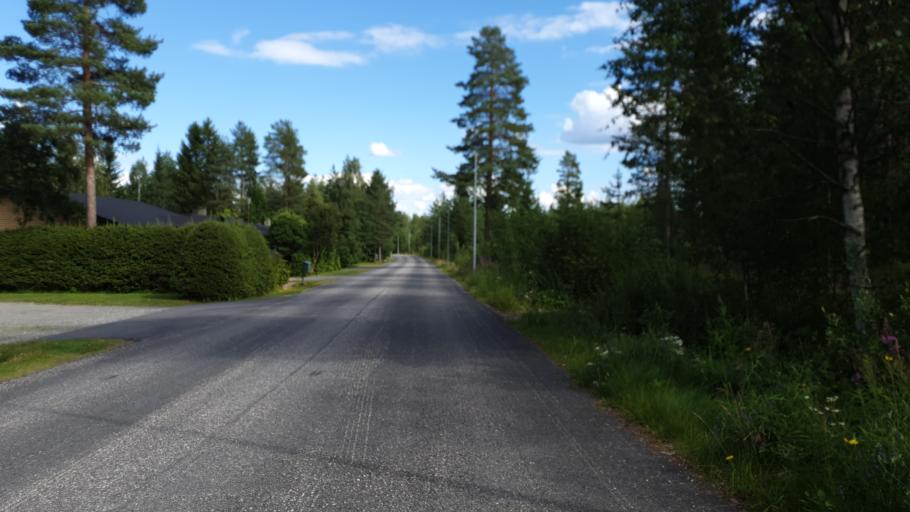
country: FI
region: Kainuu
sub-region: Kehys-Kainuu
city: Kuhmo
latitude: 64.1159
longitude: 29.5116
